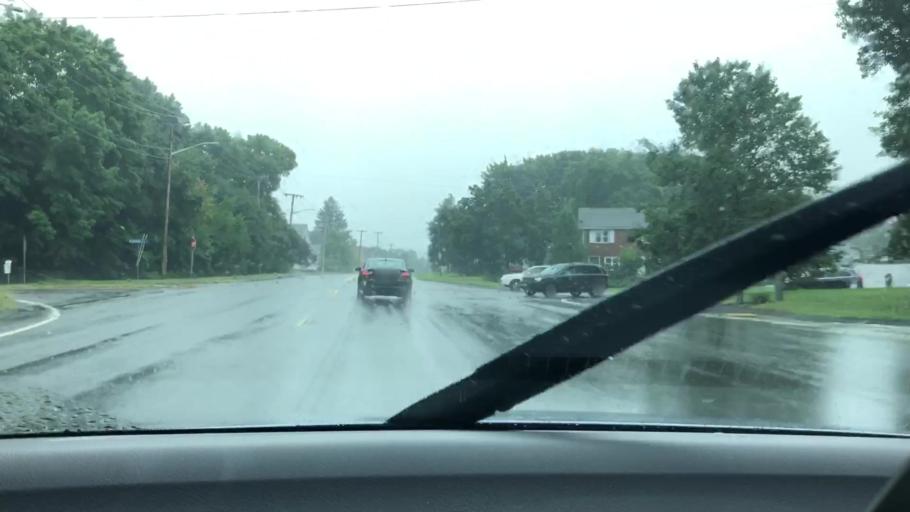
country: US
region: Massachusetts
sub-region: Norfolk County
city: Norwood
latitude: 42.2045
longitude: -71.1964
